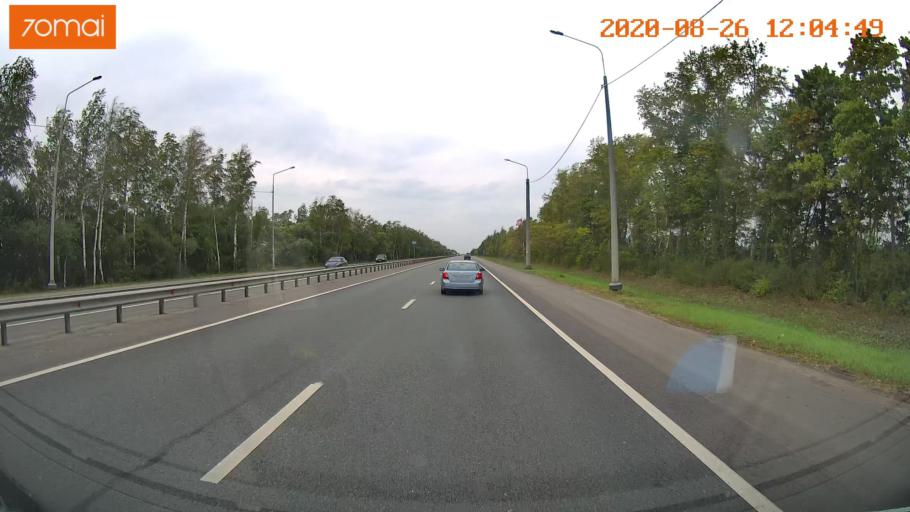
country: RU
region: Rjazan
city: Kiritsy
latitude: 54.3145
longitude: 40.1800
